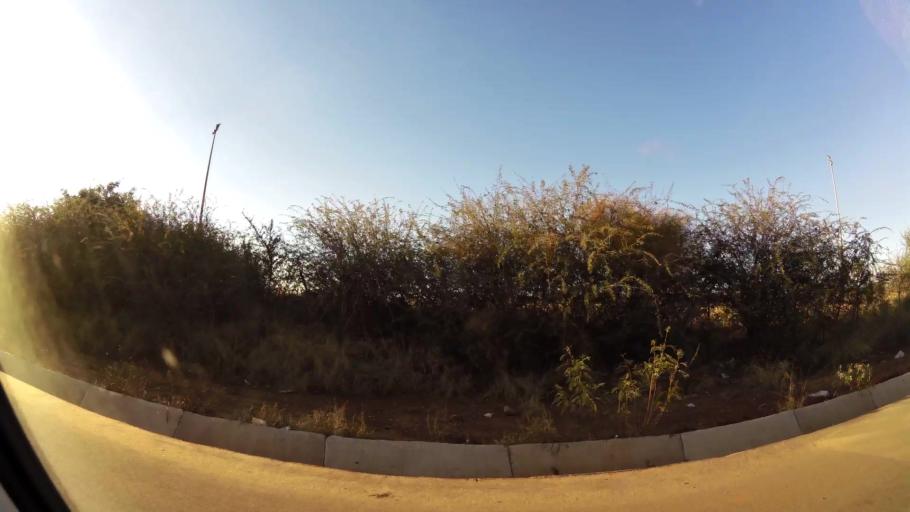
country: ZA
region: Limpopo
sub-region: Waterberg District Municipality
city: Mokopane
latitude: -24.1497
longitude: 28.9885
